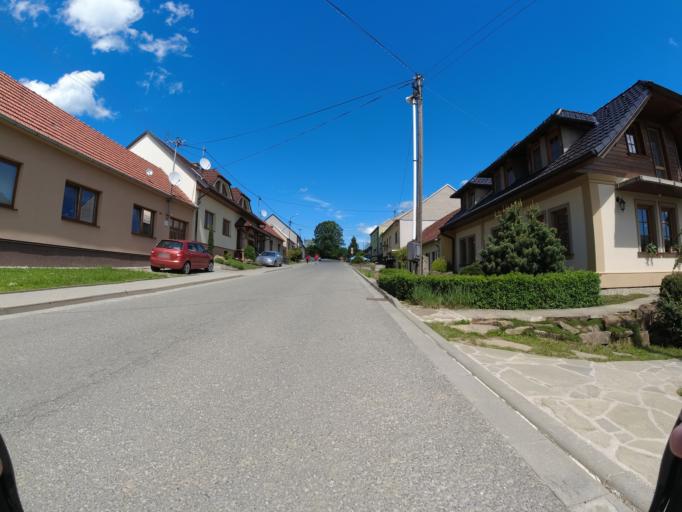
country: CZ
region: Zlin
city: Strani
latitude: 48.9080
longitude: 17.7013
